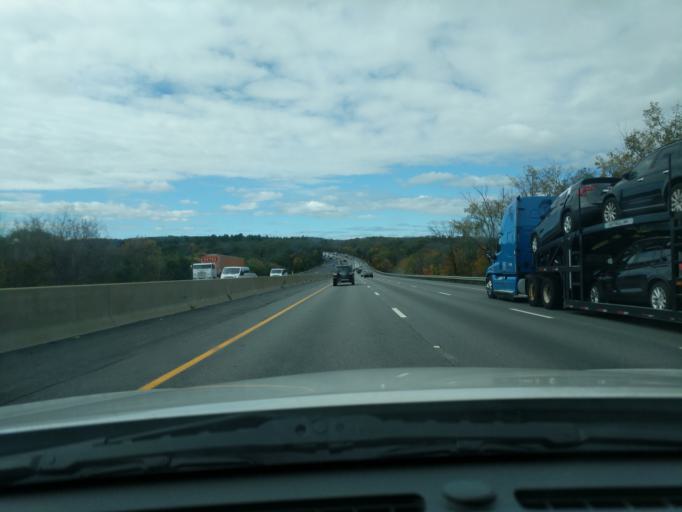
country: US
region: Massachusetts
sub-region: Worcester County
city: Grafton
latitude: 42.2281
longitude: -71.6475
